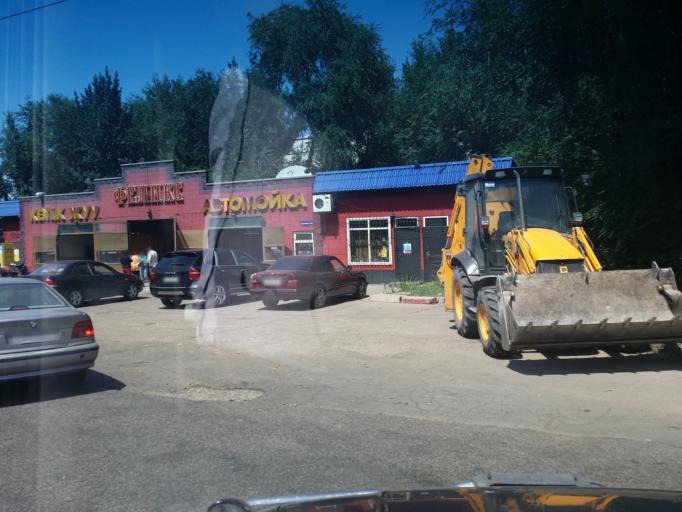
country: KZ
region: Almaty Oblysy
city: Pervomayskiy
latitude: 43.3551
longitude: 76.9477
